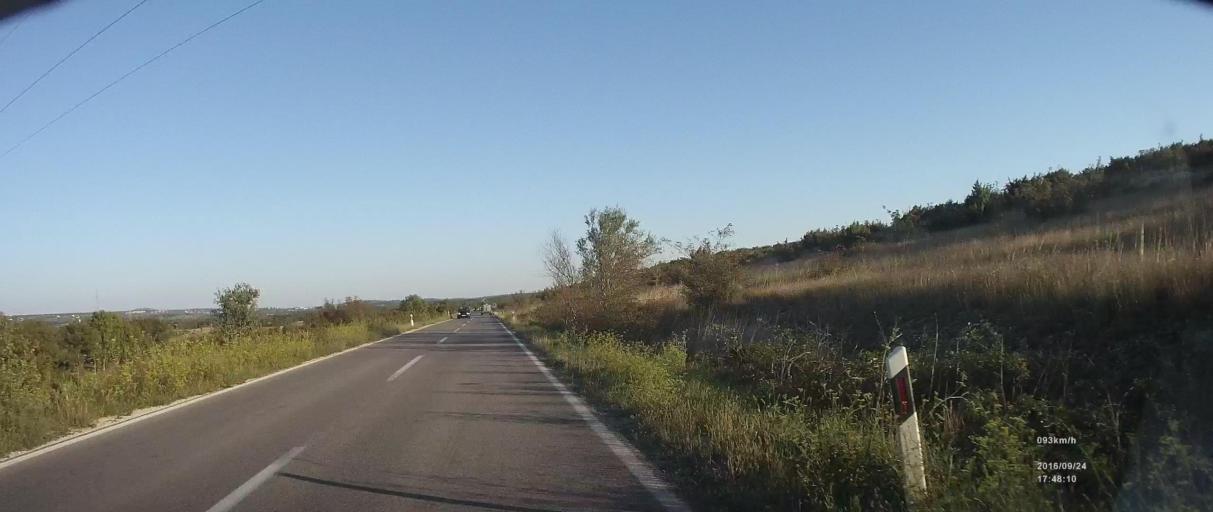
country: HR
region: Zadarska
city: Polaca
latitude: 44.0666
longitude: 15.5341
